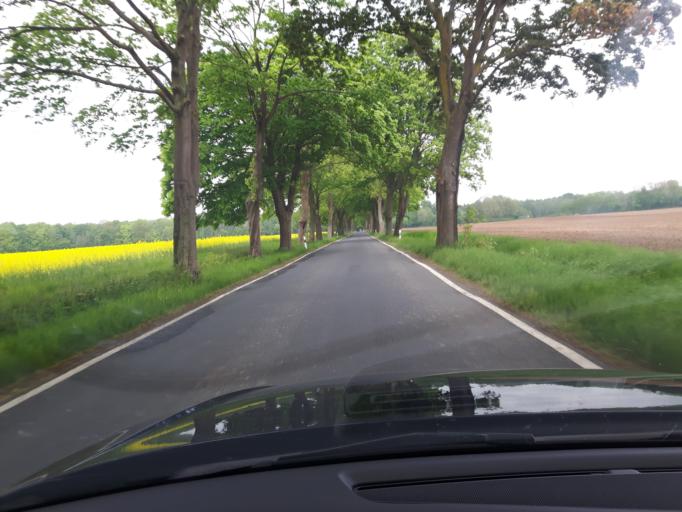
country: DE
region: Mecklenburg-Vorpommern
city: Velgast
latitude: 54.2237
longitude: 12.7335
